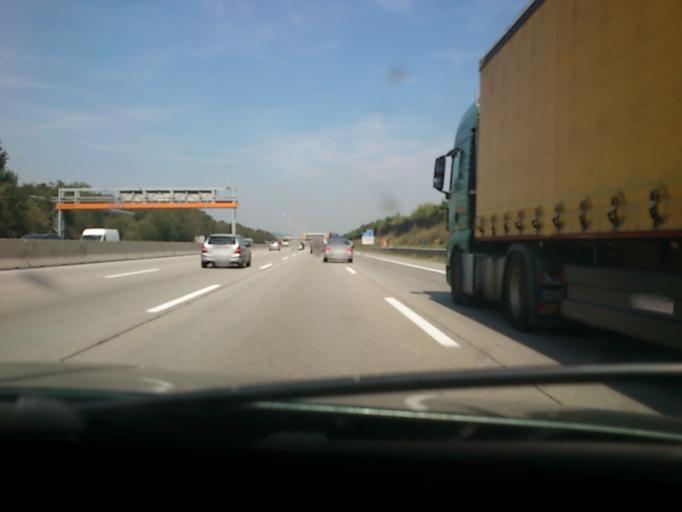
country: AT
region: Lower Austria
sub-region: Politischer Bezirk Modling
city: Biedermannsdorf
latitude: 48.0877
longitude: 16.3301
